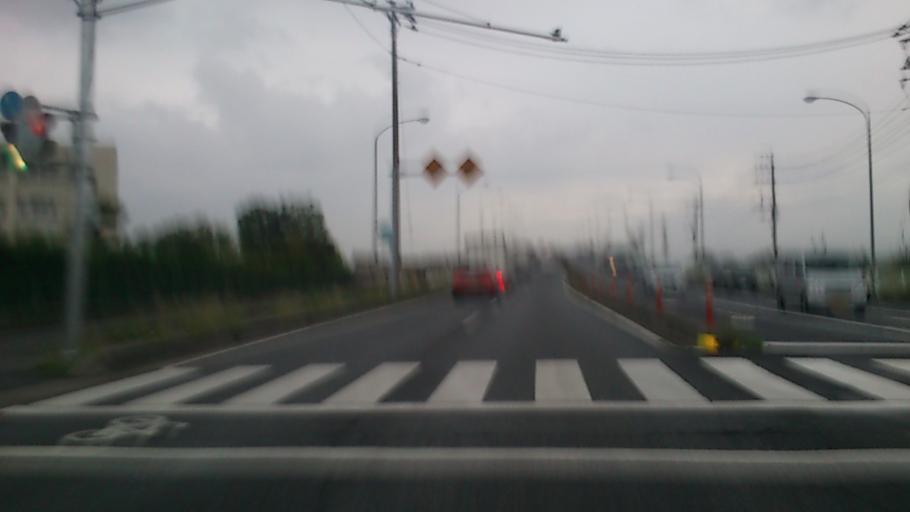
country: JP
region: Saitama
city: Hanyu
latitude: 36.1629
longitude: 139.5425
